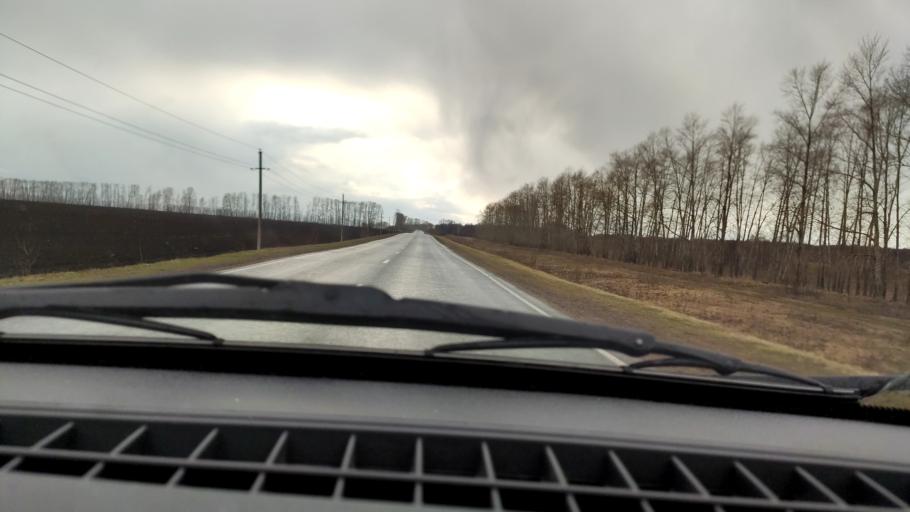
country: RU
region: Bashkortostan
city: Kushnarenkovo
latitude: 55.0608
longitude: 55.2065
